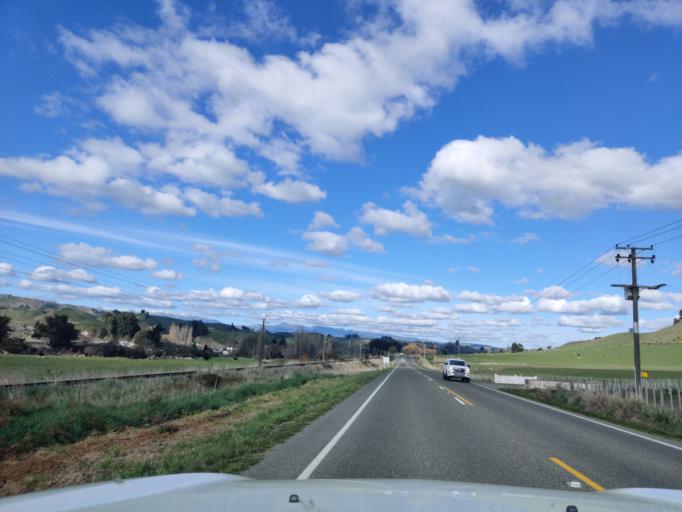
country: NZ
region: Manawatu-Wanganui
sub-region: Ruapehu District
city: Waiouru
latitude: -39.7081
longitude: 175.8344
